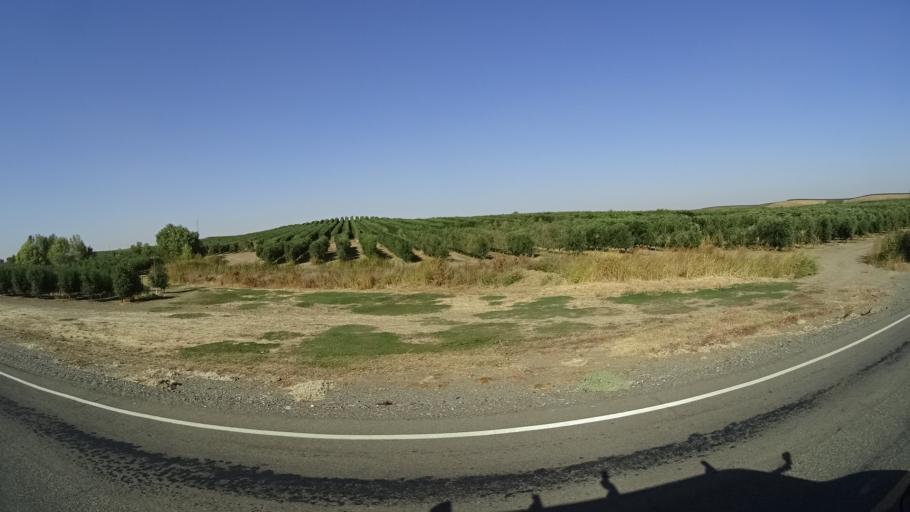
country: US
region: California
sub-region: Yolo County
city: Cottonwood
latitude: 38.7094
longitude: -121.8876
